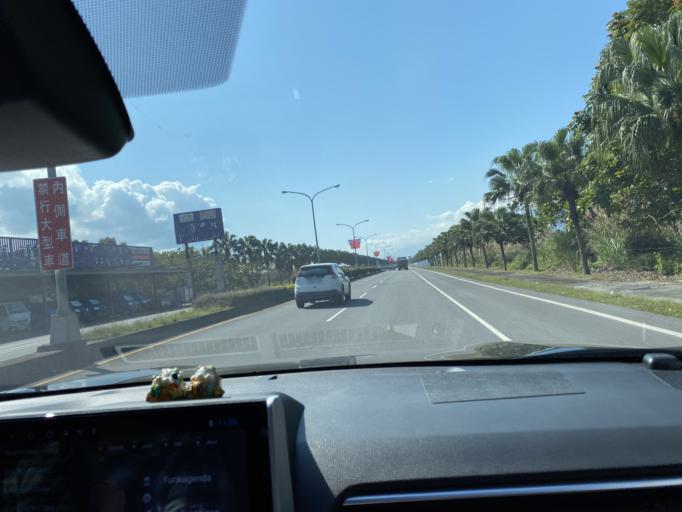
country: TW
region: Taiwan
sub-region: Hualien
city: Hualian
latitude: 23.8729
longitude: 121.5370
